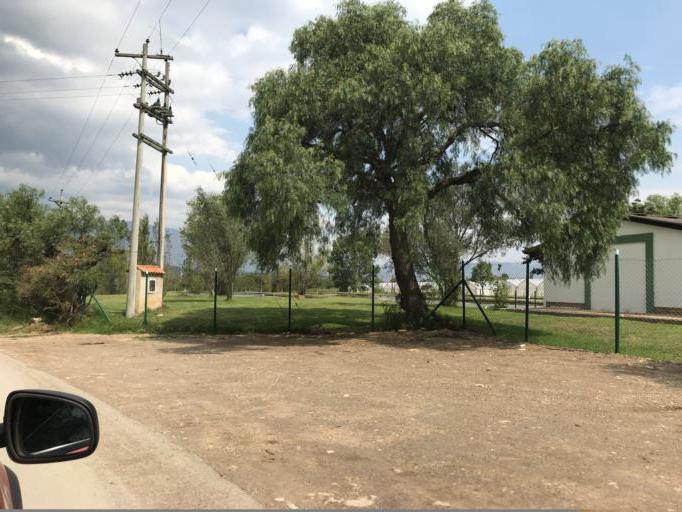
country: CO
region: Boyaca
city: Villa de Leiva
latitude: 5.6604
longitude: -73.5832
